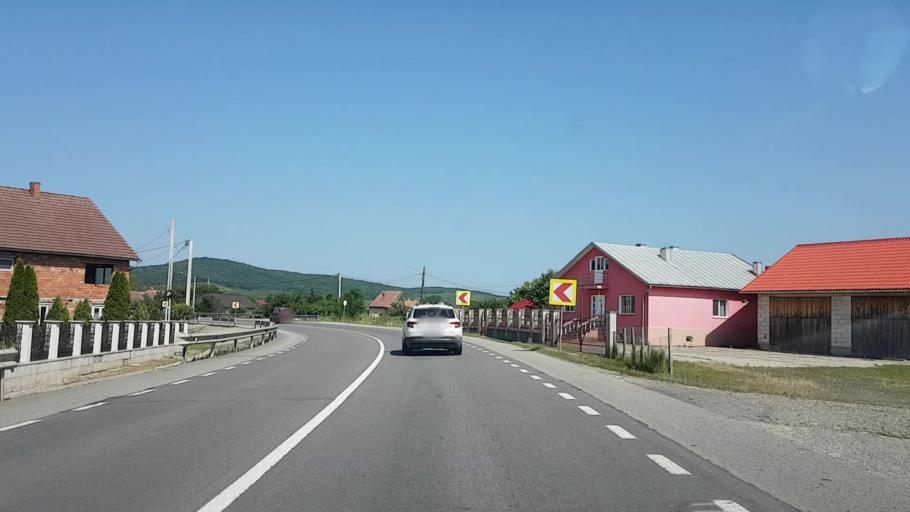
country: RO
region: Bistrita-Nasaud
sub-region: Comuna Sintereag
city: Sintereag
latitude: 47.1790
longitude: 24.2772
